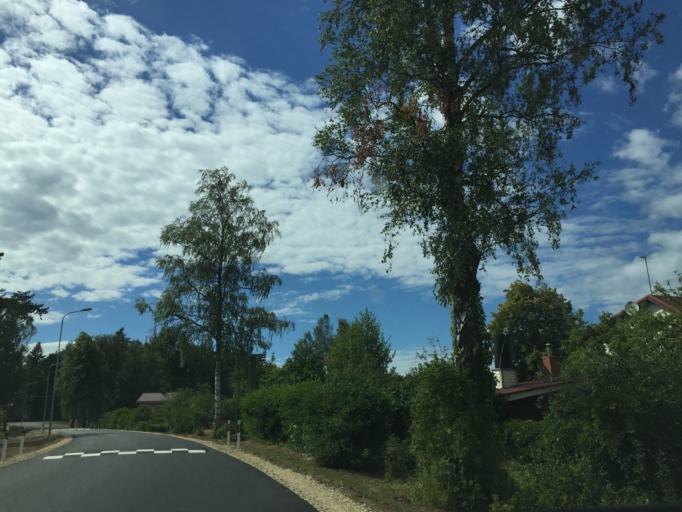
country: LV
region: Carnikava
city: Carnikava
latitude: 57.1173
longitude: 24.2309
